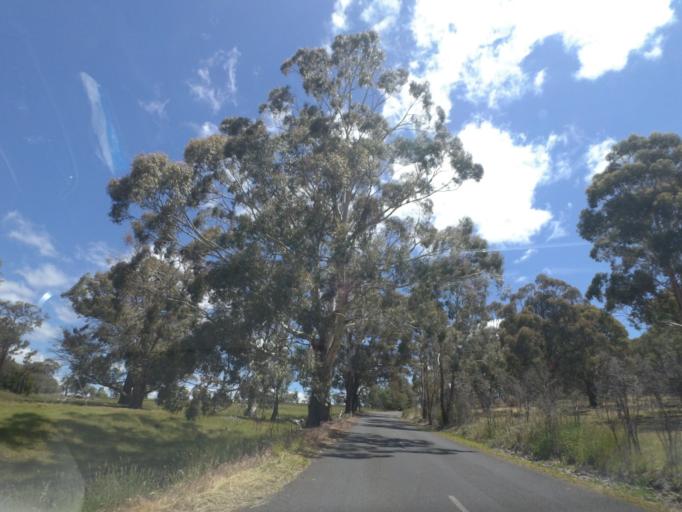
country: AU
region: Victoria
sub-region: Mount Alexander
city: Castlemaine
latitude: -37.3169
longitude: 144.1813
